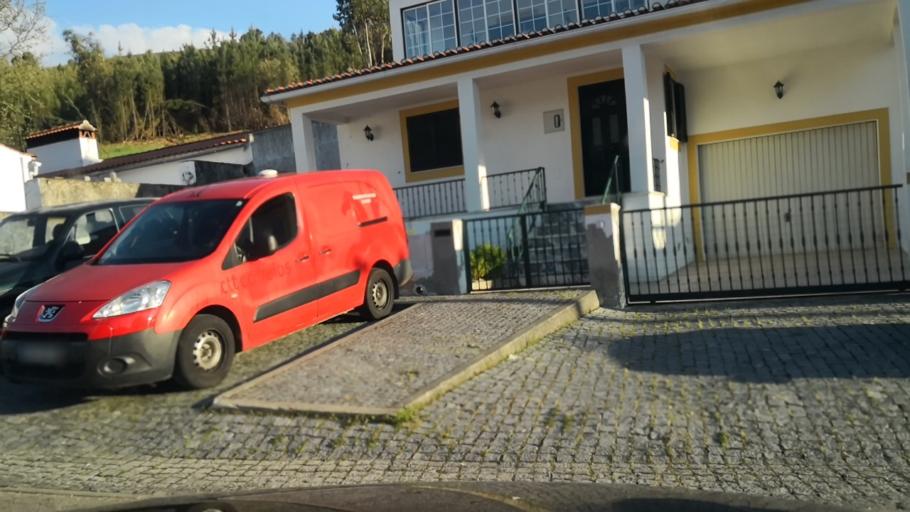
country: PT
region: Portalegre
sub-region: Marvao
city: Marvao
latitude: 39.3817
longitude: -7.3827
